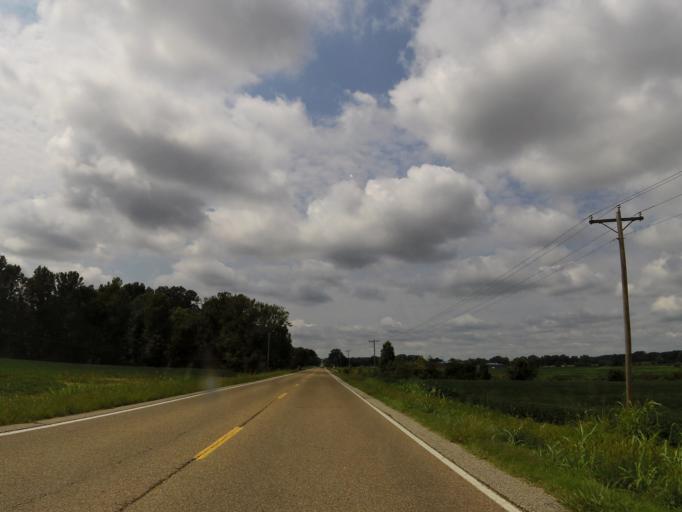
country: US
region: Tennessee
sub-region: Henderson County
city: Lexington
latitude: 35.5178
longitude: -88.2832
